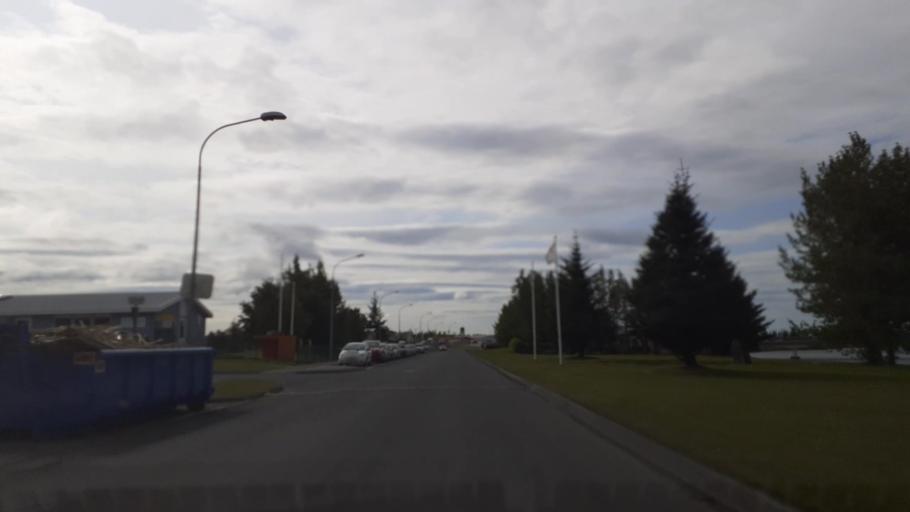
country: IS
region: South
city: Vestmannaeyjar
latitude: 63.8375
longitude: -20.4012
